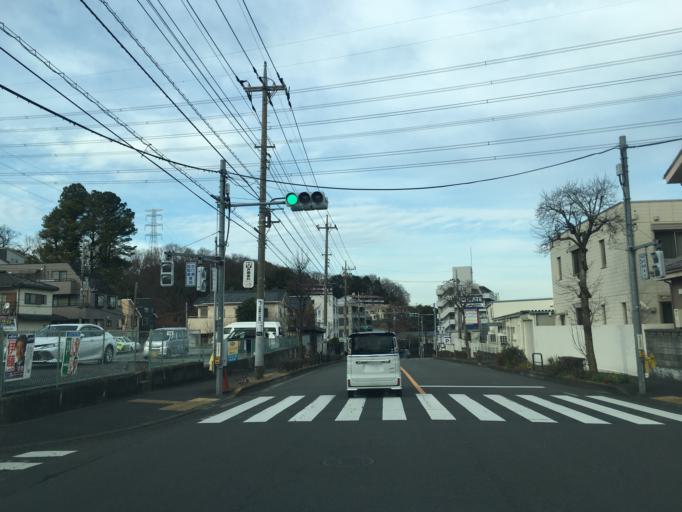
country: JP
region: Tokyo
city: Hino
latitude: 35.6238
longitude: 139.4372
